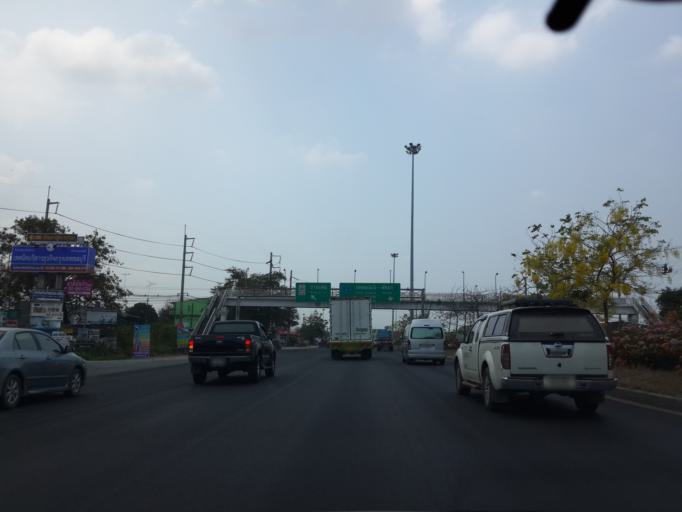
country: TH
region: Chon Buri
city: Chon Buri
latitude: 13.3389
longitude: 100.9927
